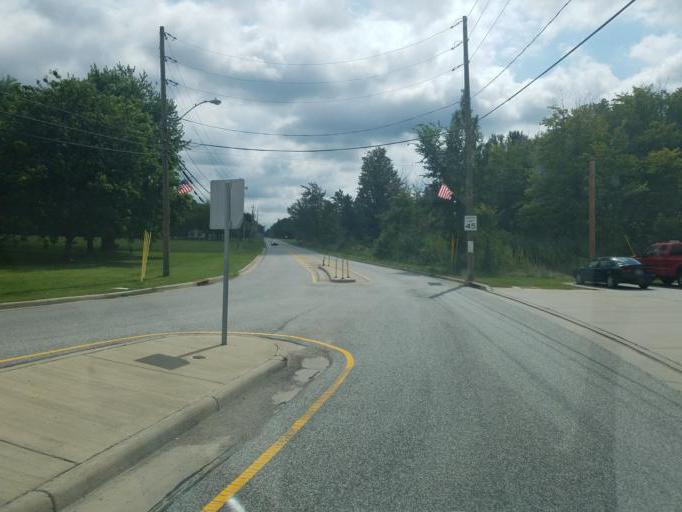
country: US
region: Ohio
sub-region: Geauga County
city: Chardon
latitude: 41.6868
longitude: -81.1756
